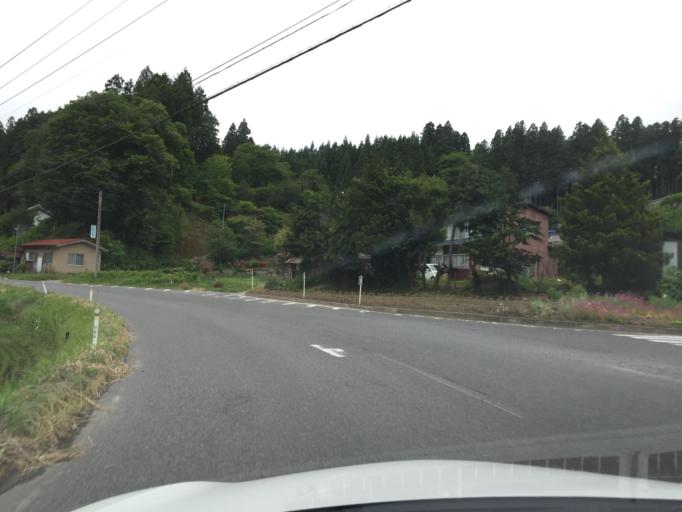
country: JP
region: Fukushima
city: Funehikimachi-funehiki
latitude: 37.3161
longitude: 140.6224
